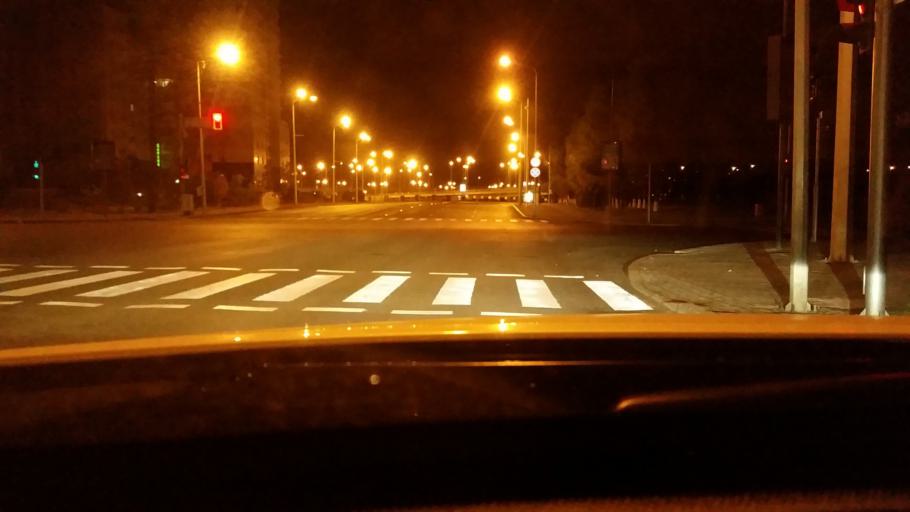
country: KZ
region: Astana Qalasy
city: Astana
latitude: 51.1291
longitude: 71.4394
